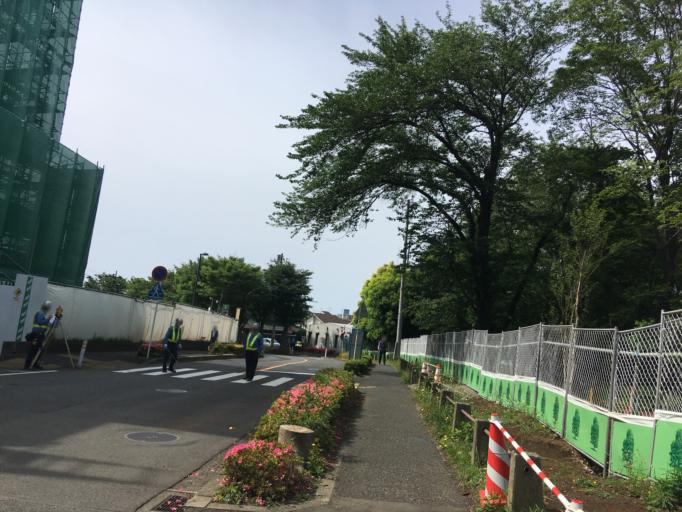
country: JP
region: Kanagawa
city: Minami-rinkan
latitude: 35.5096
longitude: 139.4694
